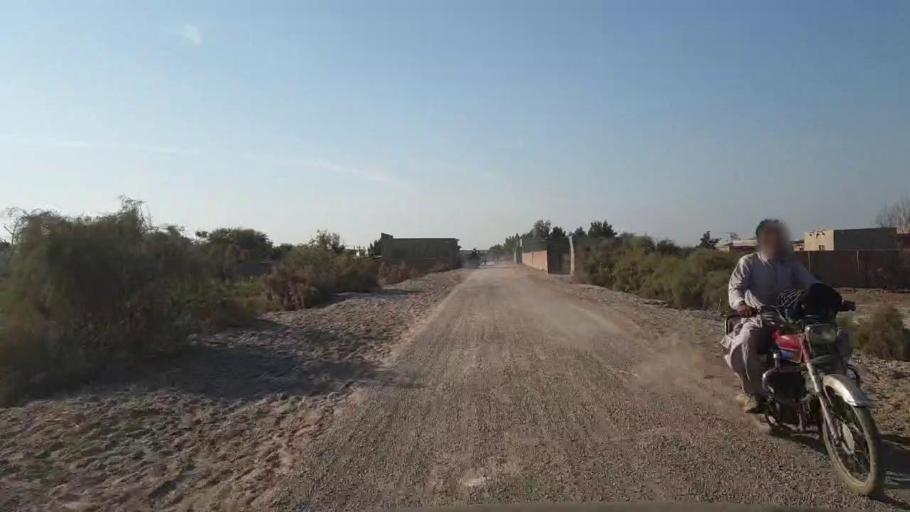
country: PK
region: Sindh
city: Shahpur Chakar
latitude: 26.1784
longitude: 68.6656
